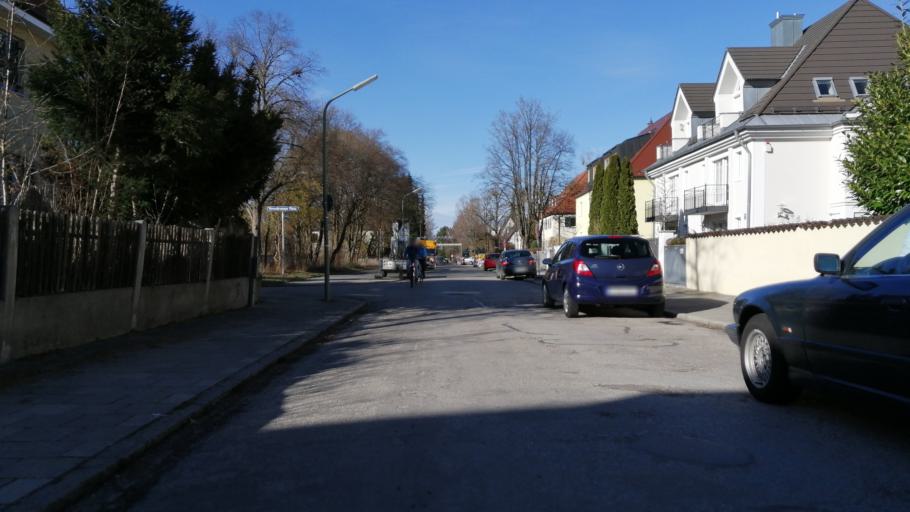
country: DE
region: Bavaria
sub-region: Upper Bavaria
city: Neuried
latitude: 48.1134
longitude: 11.5077
